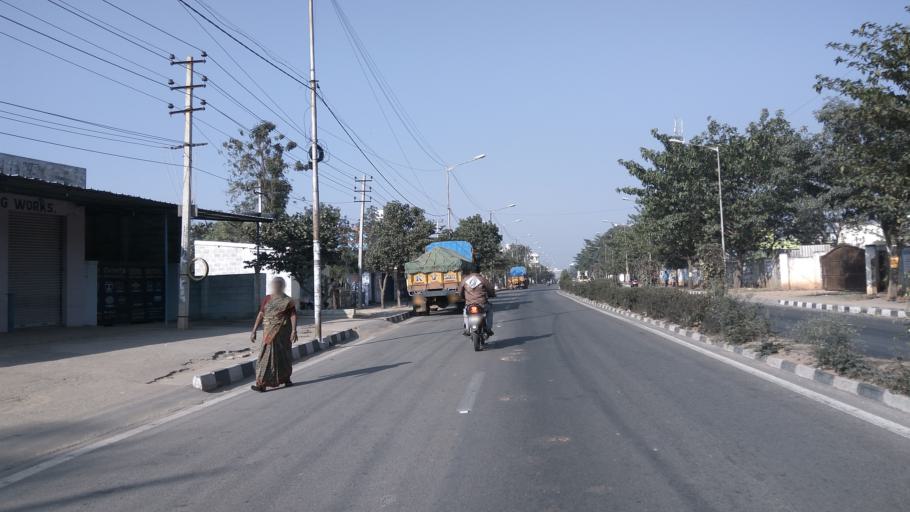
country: IN
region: Karnataka
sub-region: Bangalore Urban
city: Yelahanka
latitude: 13.1221
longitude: 77.6293
